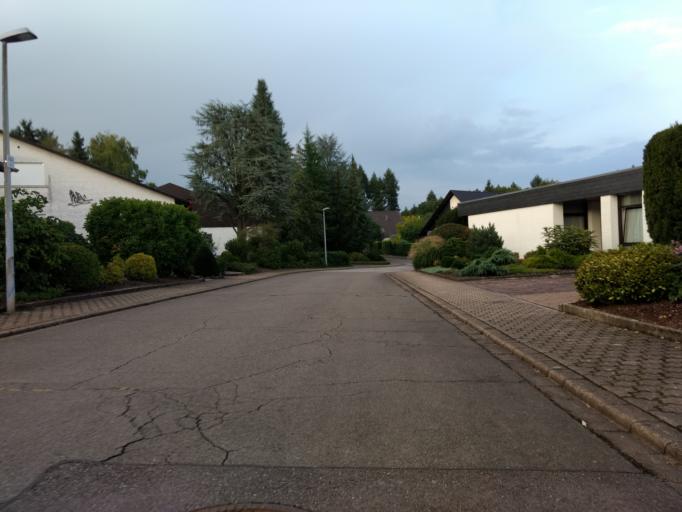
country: DE
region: Saarland
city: Dillingen
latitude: 49.3751
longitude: 6.7252
